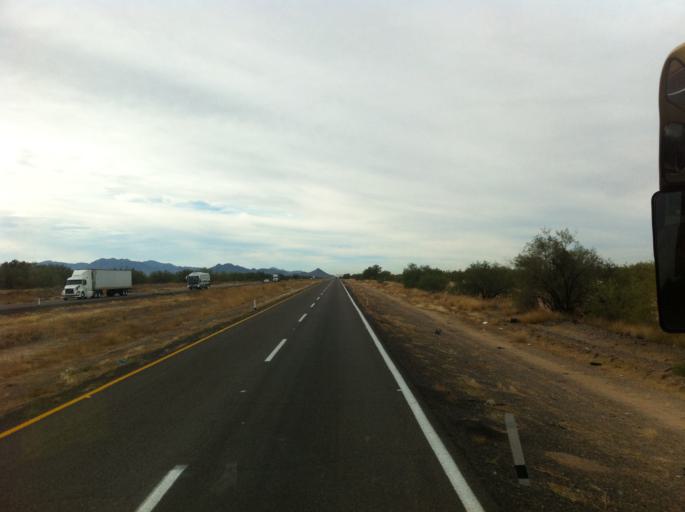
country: MX
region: Sonora
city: Hermosillo
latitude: 28.7632
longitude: -110.9695
